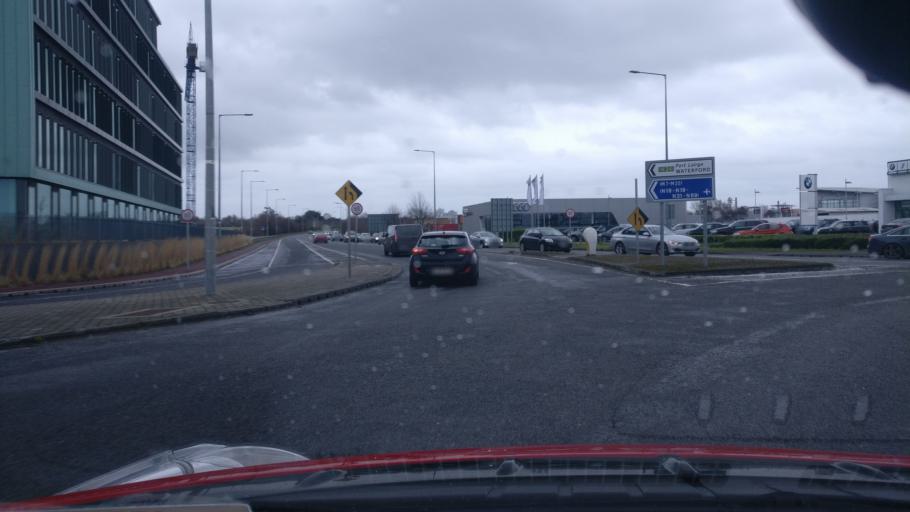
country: IE
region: Munster
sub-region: County Limerick
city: Annacotty
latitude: 52.6509
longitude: -8.5773
